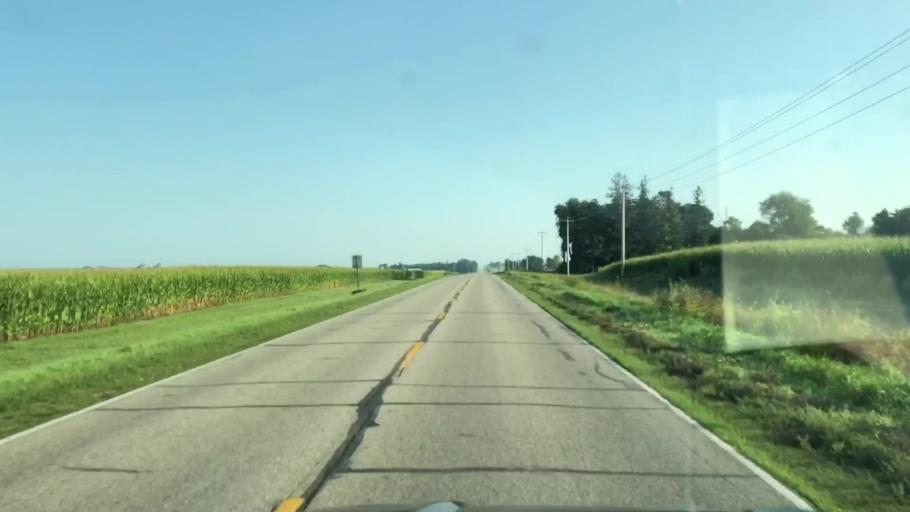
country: US
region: Iowa
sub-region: Lyon County
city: George
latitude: 43.3536
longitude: -95.9984
